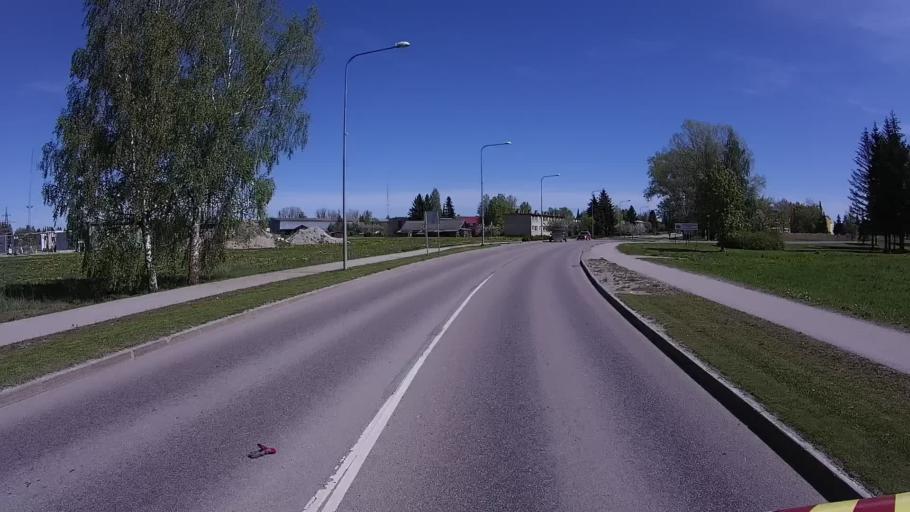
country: EE
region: Polvamaa
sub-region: Polva linn
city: Polva
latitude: 58.0686
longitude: 27.0767
